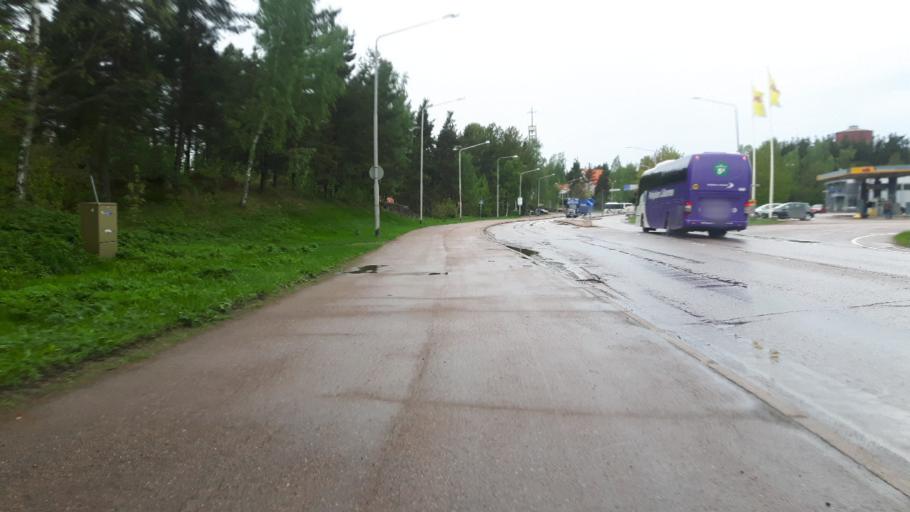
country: FI
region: Kymenlaakso
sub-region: Kotka-Hamina
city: Kotka
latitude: 60.4856
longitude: 26.9066
